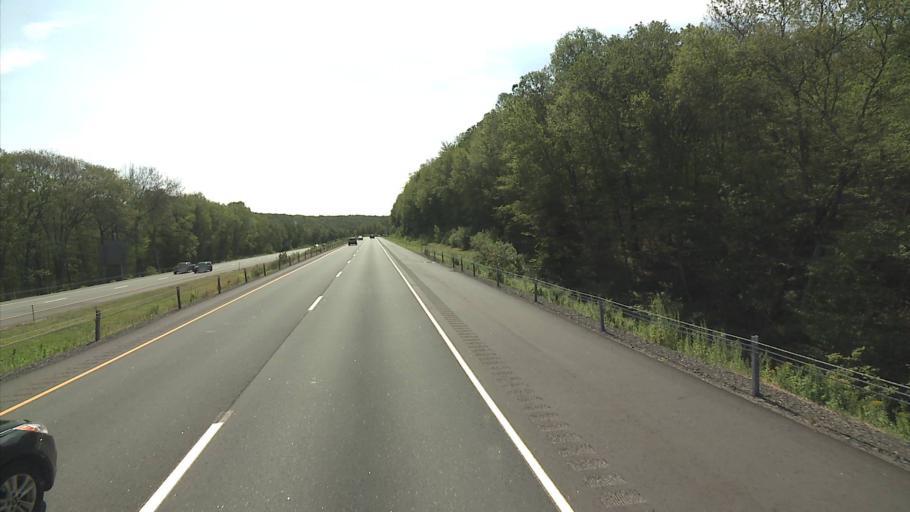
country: US
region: Connecticut
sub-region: Hartford County
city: Terramuggus
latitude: 41.6291
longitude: -72.4490
